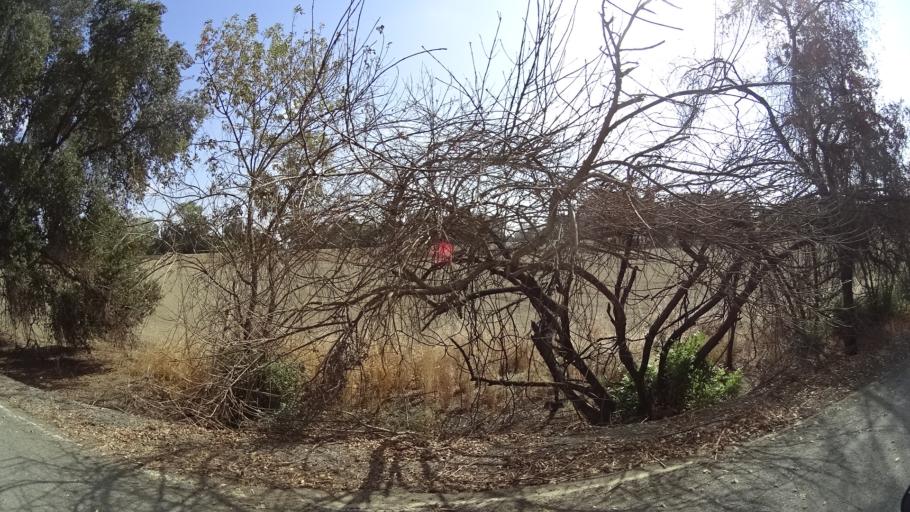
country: US
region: California
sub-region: Yolo County
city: Woodland
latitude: 38.7747
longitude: -121.6895
